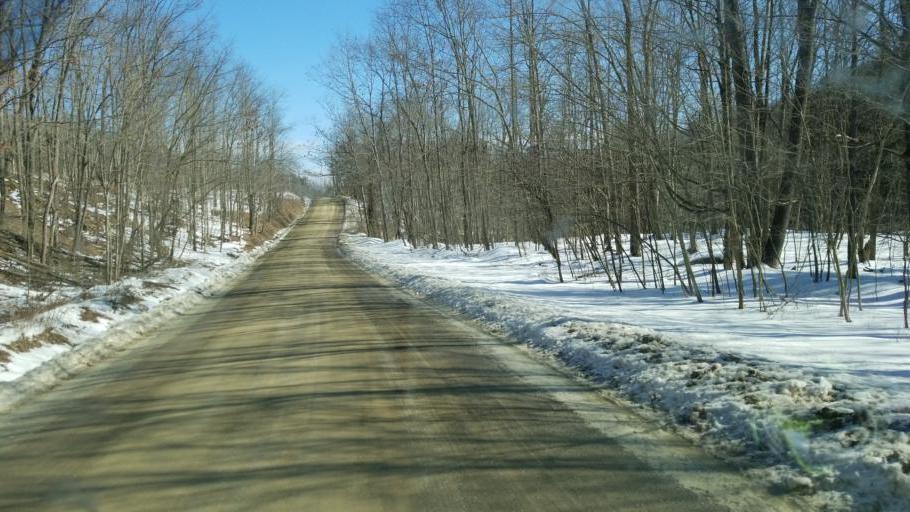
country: US
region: New York
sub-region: Allegany County
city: Alfred
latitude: 42.2478
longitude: -77.7058
